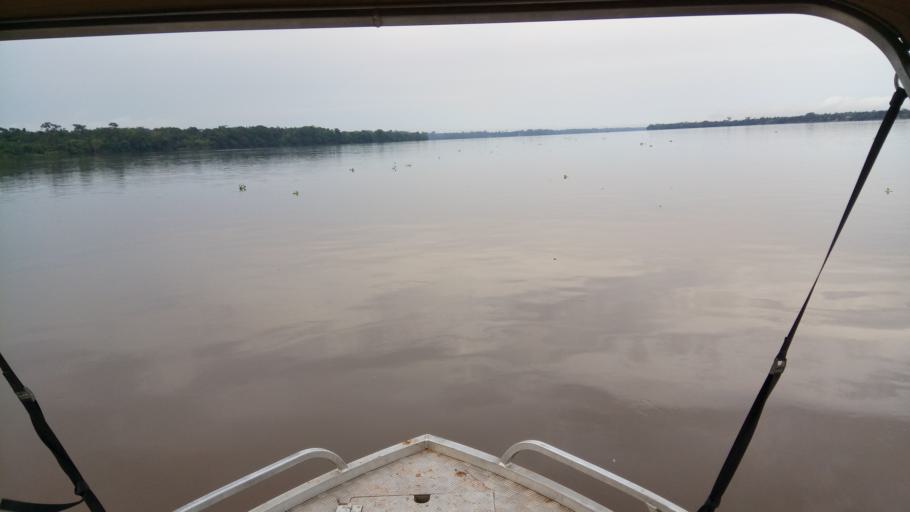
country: CD
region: Eastern Province
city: Kisangani
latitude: 0.5746
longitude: 24.8094
